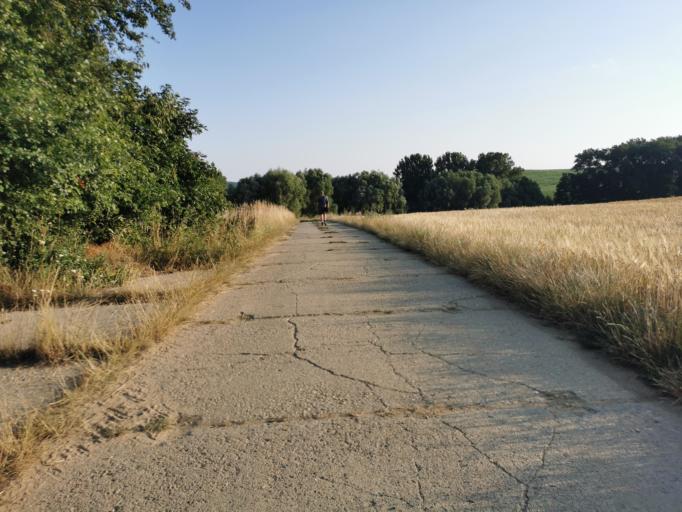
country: SK
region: Trnavsky
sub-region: Okres Skalica
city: Skalica
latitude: 48.7878
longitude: 17.2782
